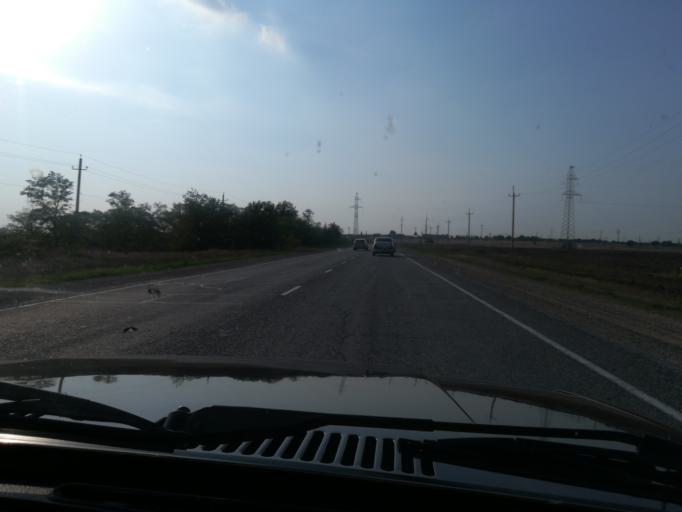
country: RU
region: Krasnodarskiy
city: Yurovka
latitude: 45.1026
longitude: 37.4253
